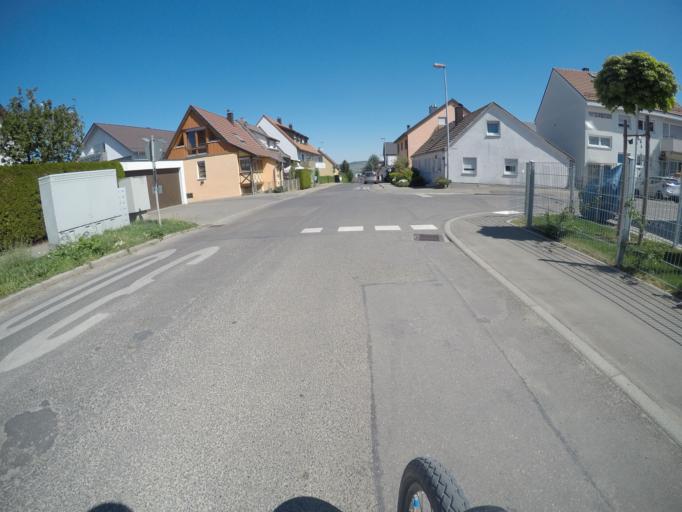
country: DE
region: Baden-Wuerttemberg
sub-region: Regierungsbezirk Stuttgart
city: Waiblingen
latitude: 48.8034
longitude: 9.3195
